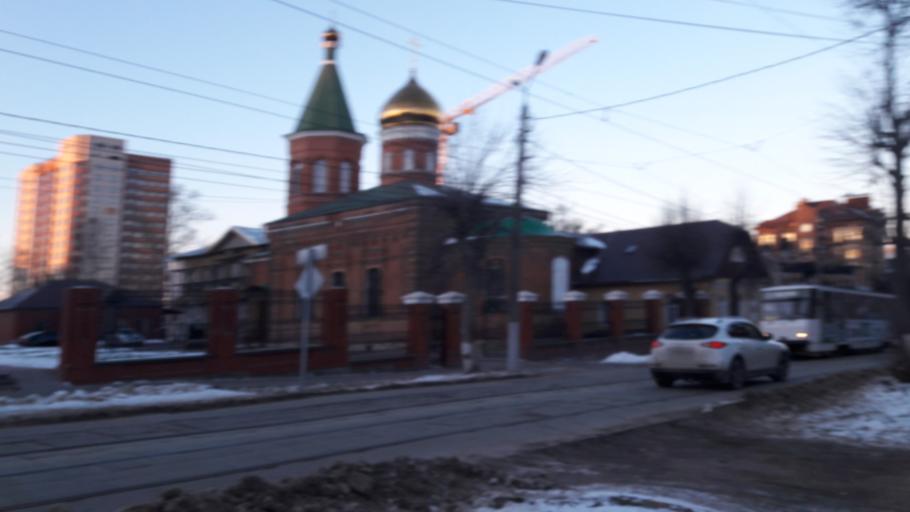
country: RU
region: Tula
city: Tula
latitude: 54.1868
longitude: 37.6068
